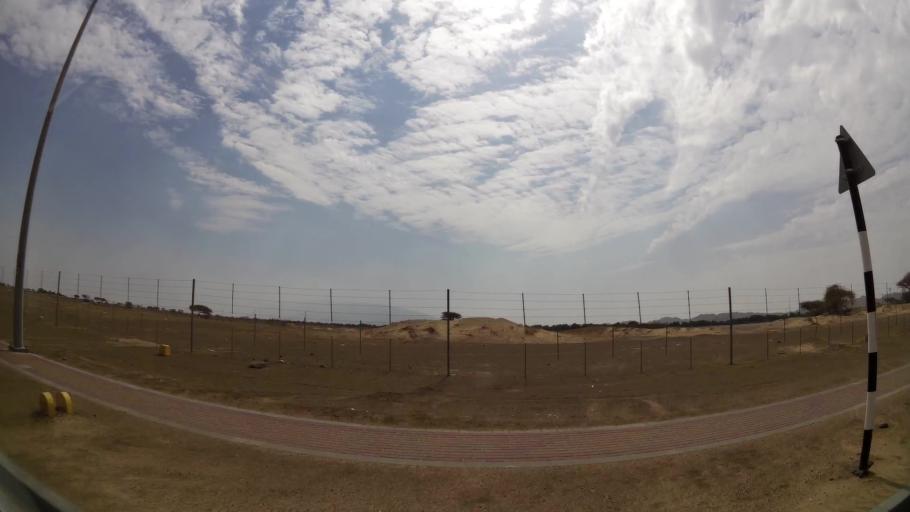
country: AE
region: Abu Dhabi
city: Al Ain
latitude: 24.1859
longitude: 55.7994
